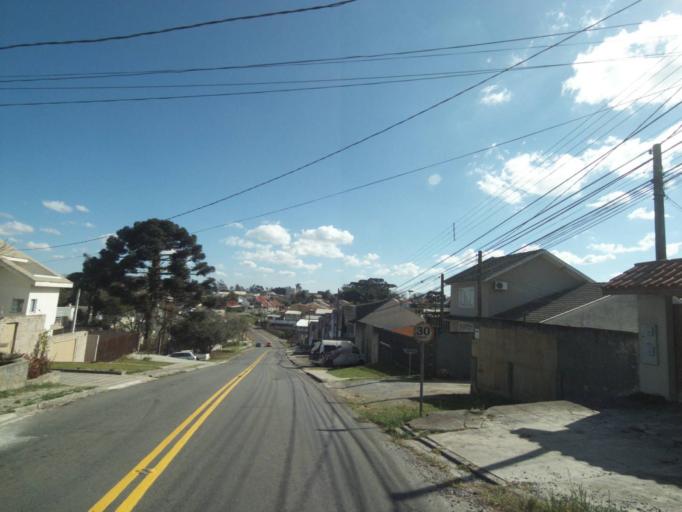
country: BR
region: Parana
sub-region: Curitiba
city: Curitiba
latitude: -25.3853
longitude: -49.2575
